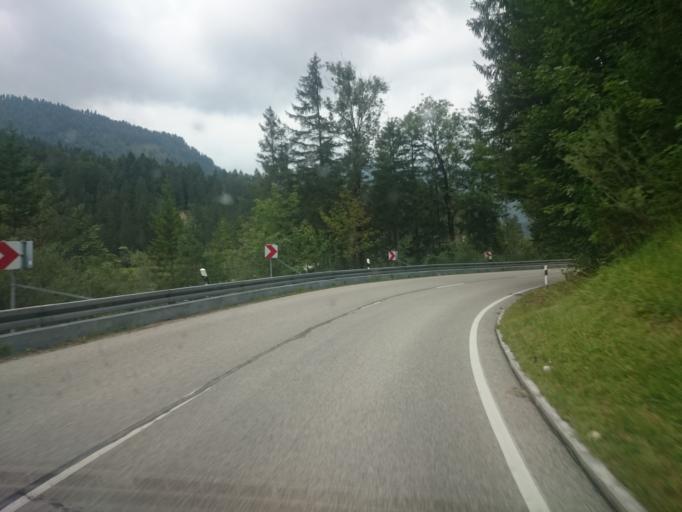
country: DE
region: Bavaria
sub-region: Upper Bavaria
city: Jachenau
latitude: 47.5308
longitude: 11.4396
